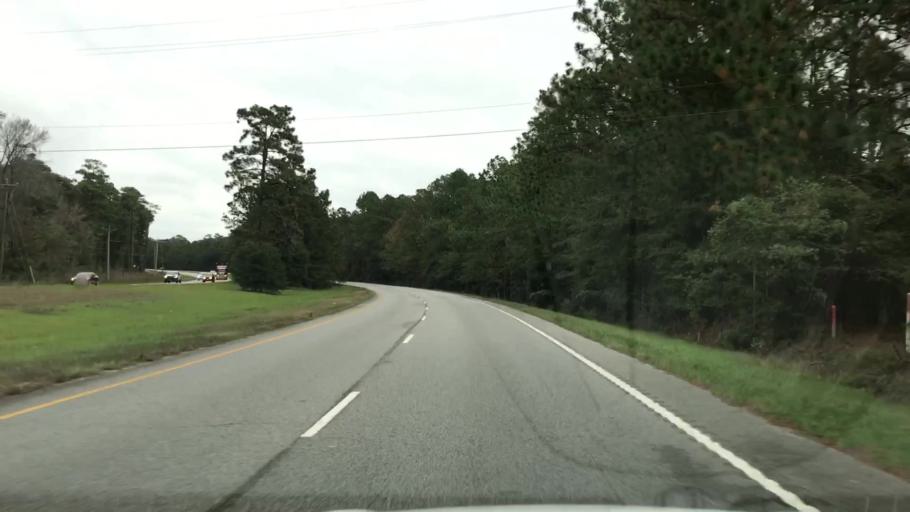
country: US
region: South Carolina
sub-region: Georgetown County
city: Georgetown
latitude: 33.3646
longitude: -79.2258
